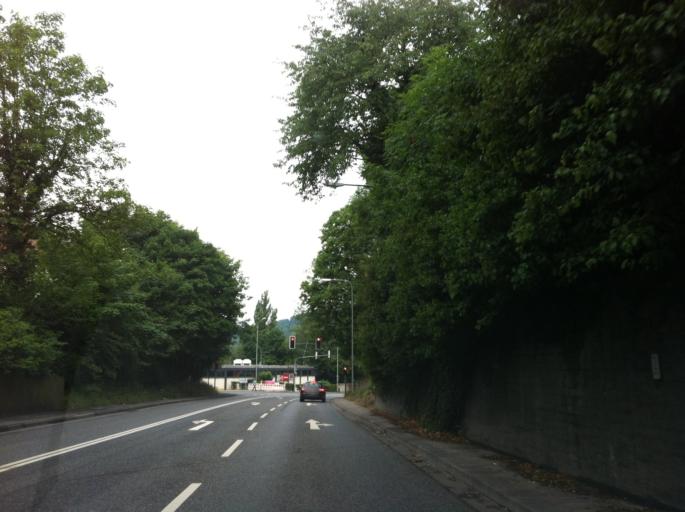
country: DE
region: Hesse
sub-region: Regierungsbezirk Darmstadt
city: Konigstein im Taunus
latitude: 50.1832
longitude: 8.4707
